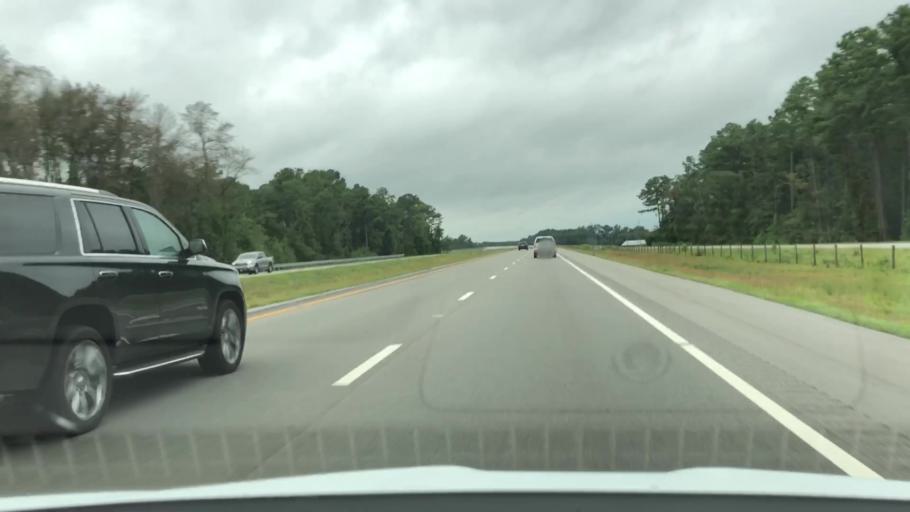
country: US
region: North Carolina
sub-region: Wayne County
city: Elroy
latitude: 35.3500
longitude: -77.8472
